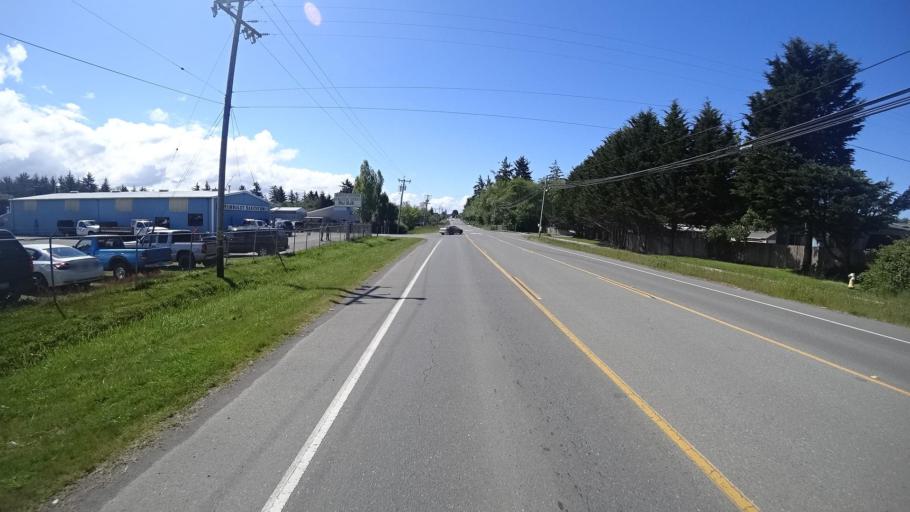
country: US
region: California
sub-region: Humboldt County
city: McKinleyville
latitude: 40.9526
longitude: -124.1008
